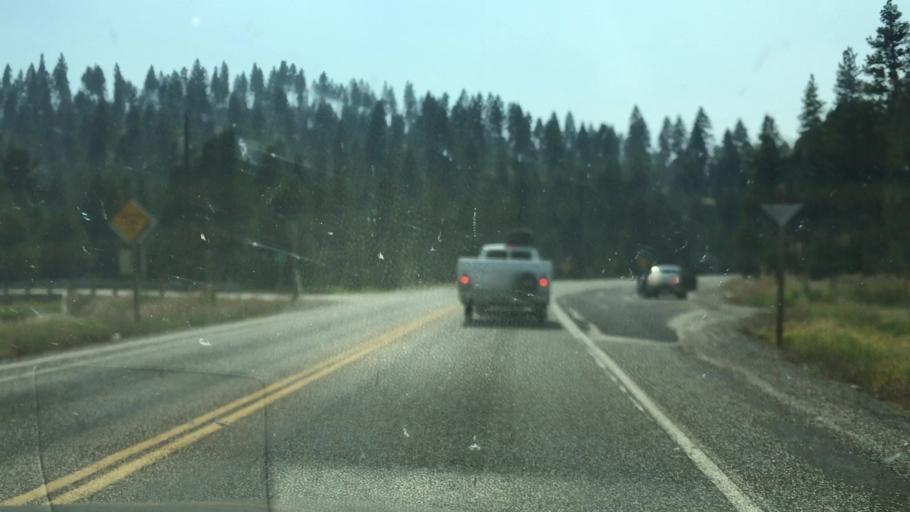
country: US
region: Idaho
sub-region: Valley County
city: Cascade
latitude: 44.3357
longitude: -116.0354
